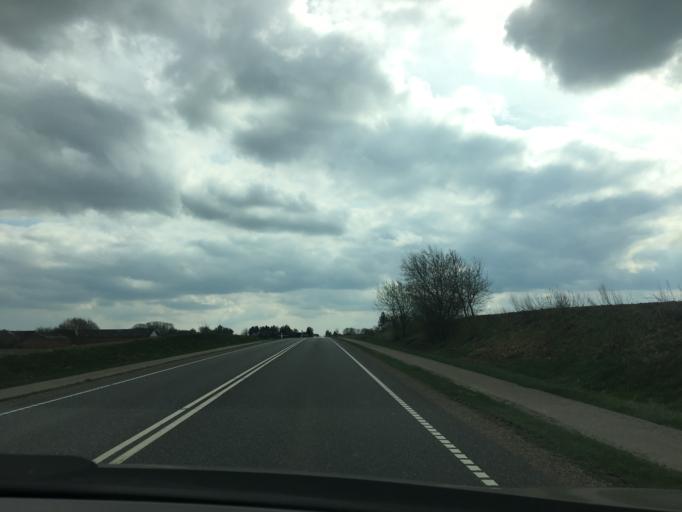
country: DK
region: Central Jutland
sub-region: Horsens Kommune
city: Braedstrup
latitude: 55.9946
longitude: 9.6044
